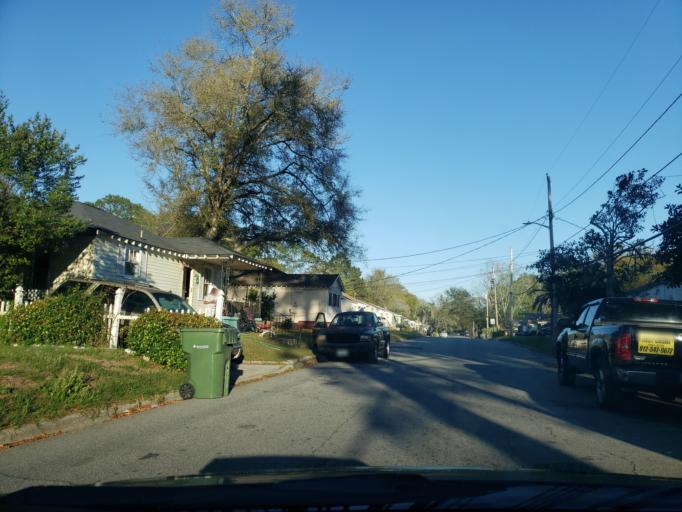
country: US
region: Georgia
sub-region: Chatham County
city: Thunderbolt
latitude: 32.0544
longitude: -81.0601
